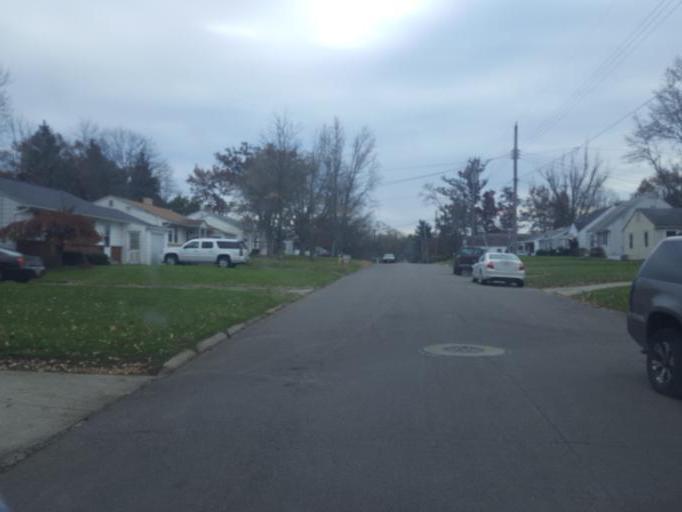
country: US
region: Ohio
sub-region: Richland County
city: Ontario
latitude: 40.7555
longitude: -82.5546
